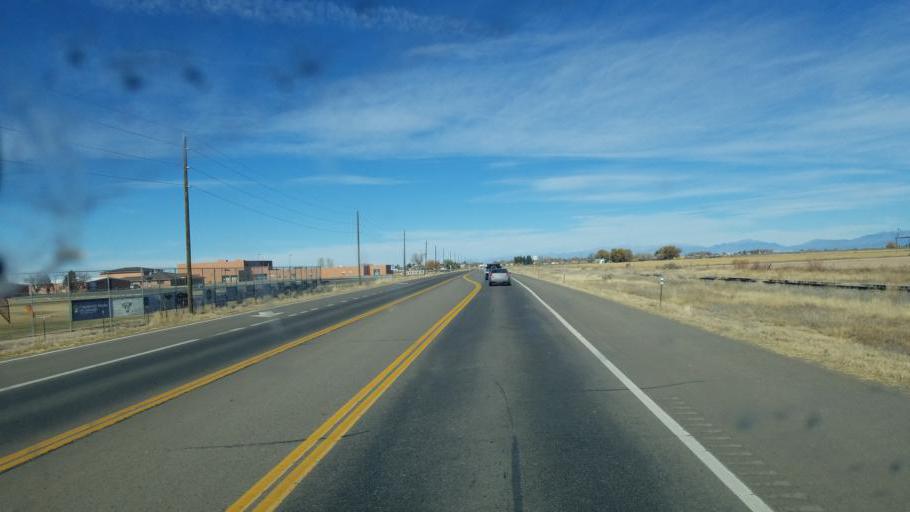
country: US
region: Colorado
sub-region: Conejos County
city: Conejos
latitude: 37.2457
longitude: -105.9689
